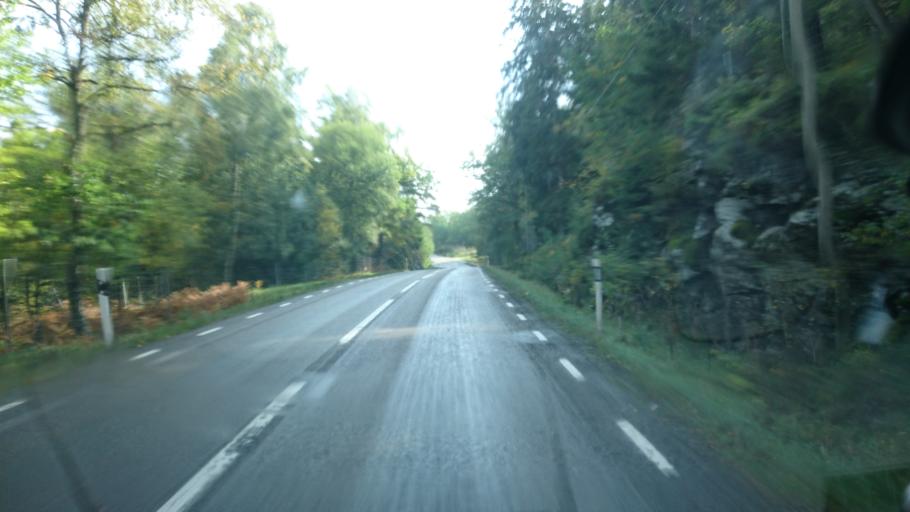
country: SE
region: Vaestra Goetaland
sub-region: Alingsas Kommun
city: Sollebrunn
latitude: 58.1363
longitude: 12.4554
